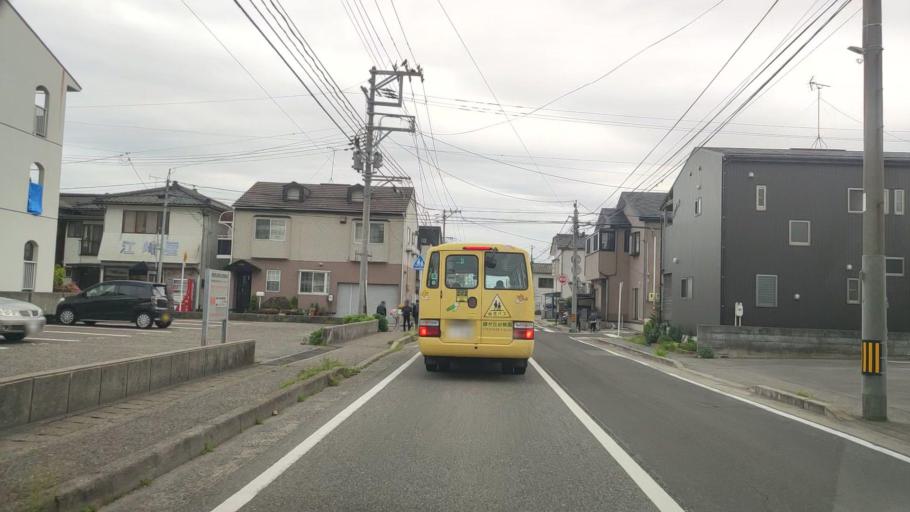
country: JP
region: Niigata
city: Niigata-shi
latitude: 37.9422
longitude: 139.0786
